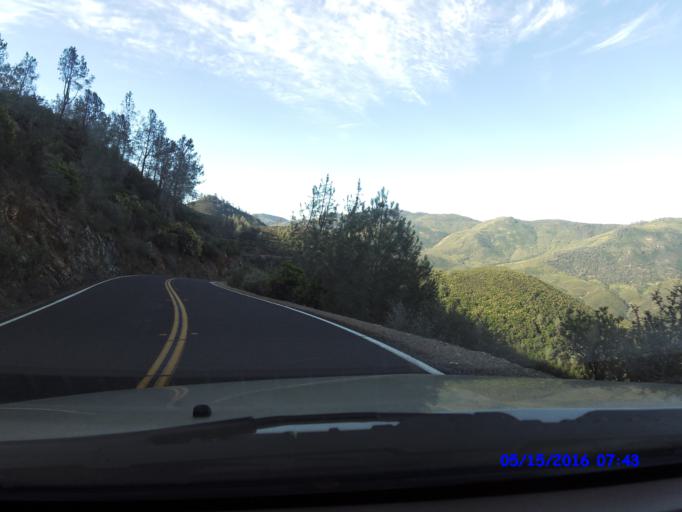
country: US
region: California
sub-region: Mariposa County
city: Mariposa
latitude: 37.6473
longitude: -120.1475
